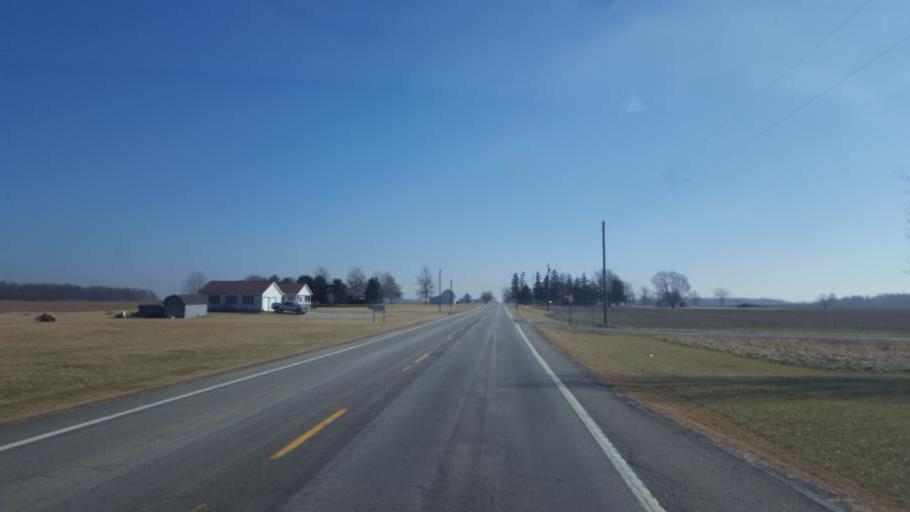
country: US
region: Ohio
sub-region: Huron County
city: Willard
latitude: 41.0444
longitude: -82.8023
